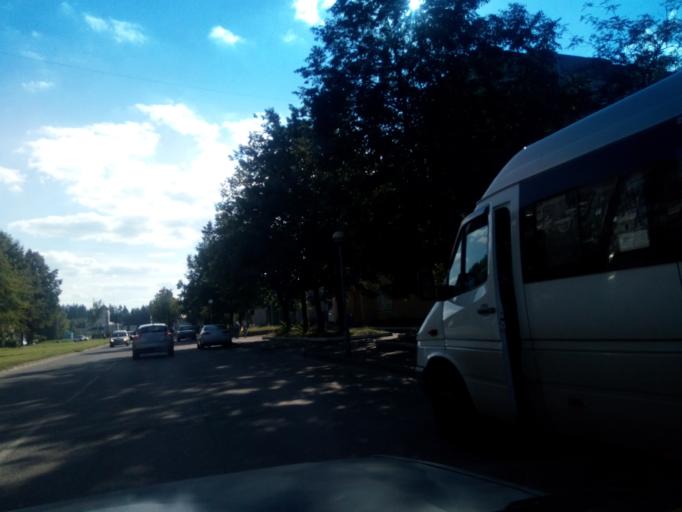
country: BY
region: Vitebsk
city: Navapolatsk
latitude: 55.5236
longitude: 28.6650
